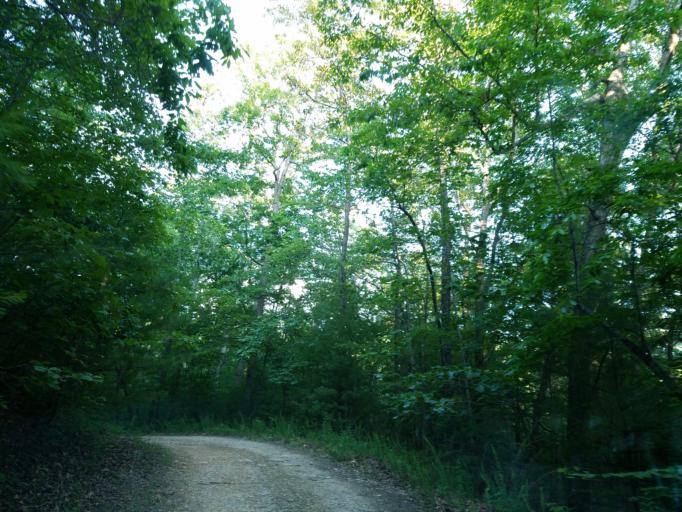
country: US
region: Georgia
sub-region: Fannin County
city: Blue Ridge
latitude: 34.8148
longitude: -84.1459
